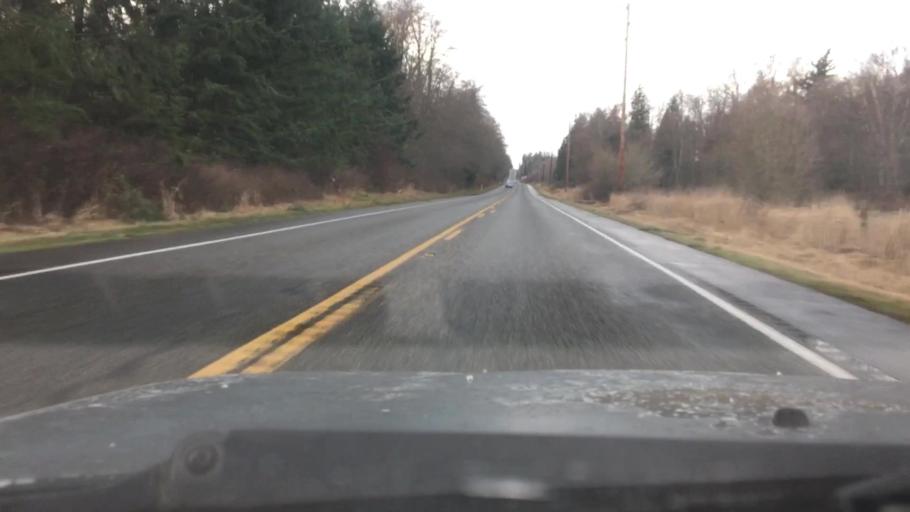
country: US
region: Washington
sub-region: Whatcom County
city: Ferndale
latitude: 48.8195
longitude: -122.6485
